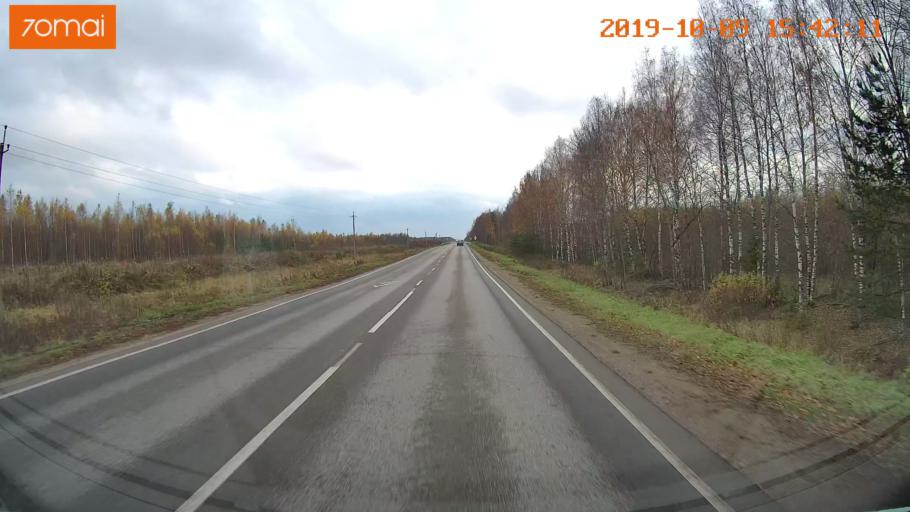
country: RU
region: Kostroma
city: Oktyabr'skiy
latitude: 57.8710
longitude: 41.1117
